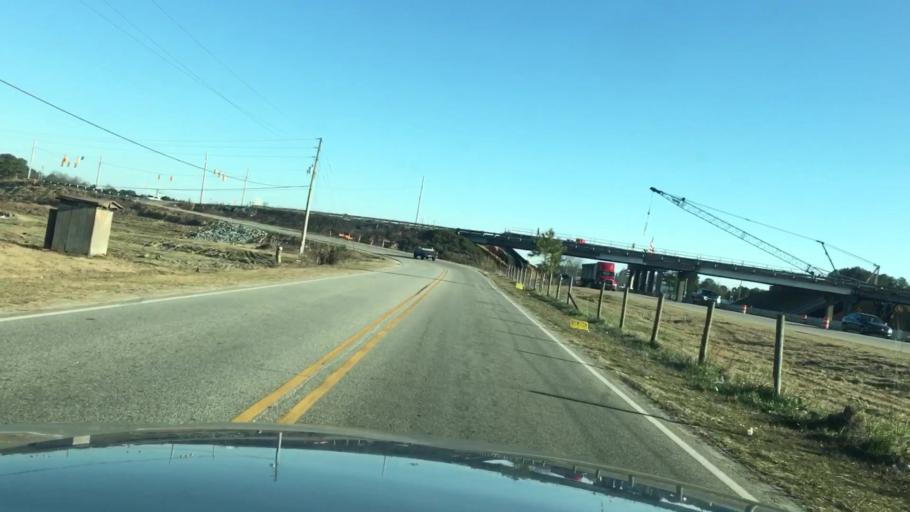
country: US
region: North Carolina
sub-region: Cumberland County
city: Hope Mills
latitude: 34.9439
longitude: -78.9321
